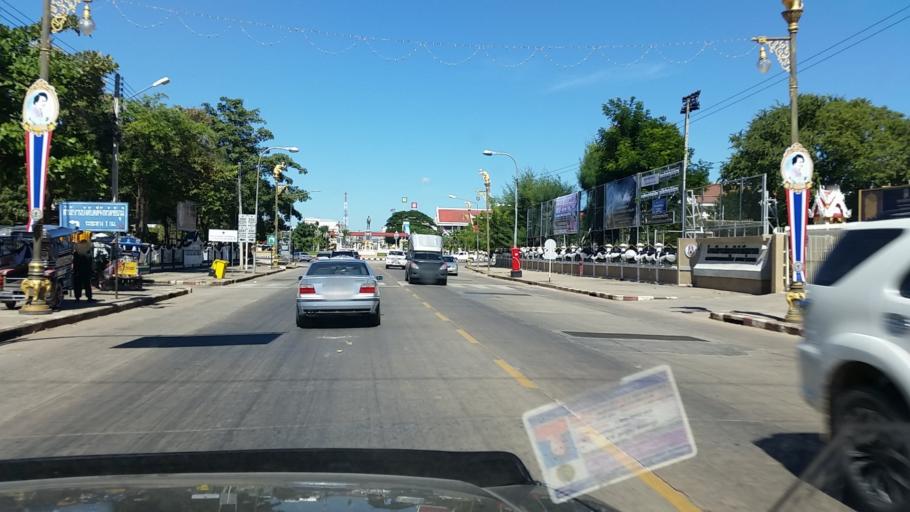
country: TH
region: Chaiyaphum
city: Chaiyaphum
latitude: 15.8054
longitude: 102.0314
